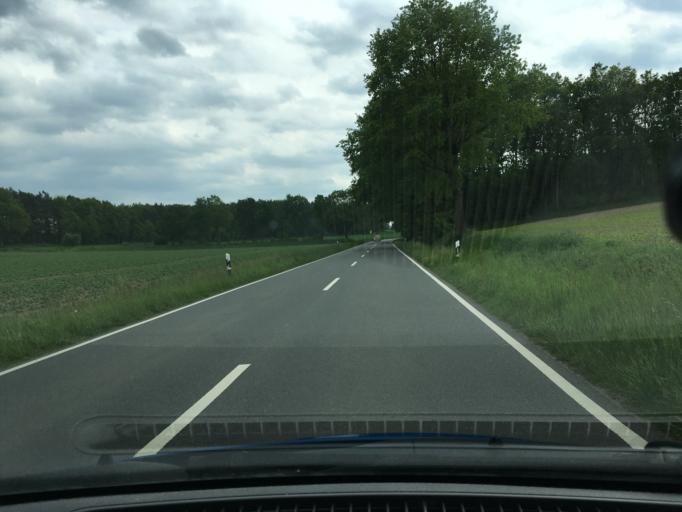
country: DE
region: Lower Saxony
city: Betzendorf
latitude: 53.1206
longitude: 10.3091
